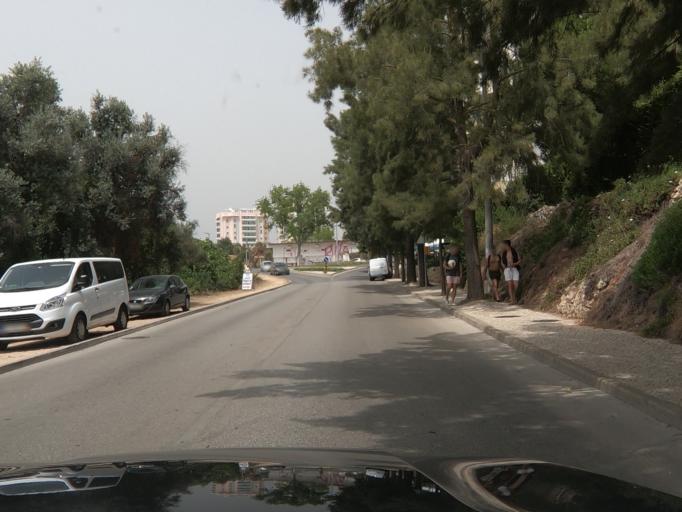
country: PT
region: Faro
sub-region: Portimao
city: Portimao
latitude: 37.1243
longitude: -8.5417
